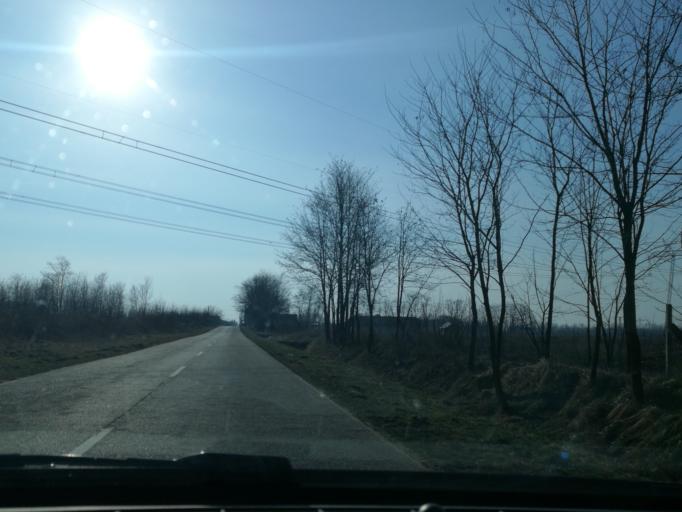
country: HU
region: Szabolcs-Szatmar-Bereg
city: Levelek
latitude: 47.9800
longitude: 21.9716
